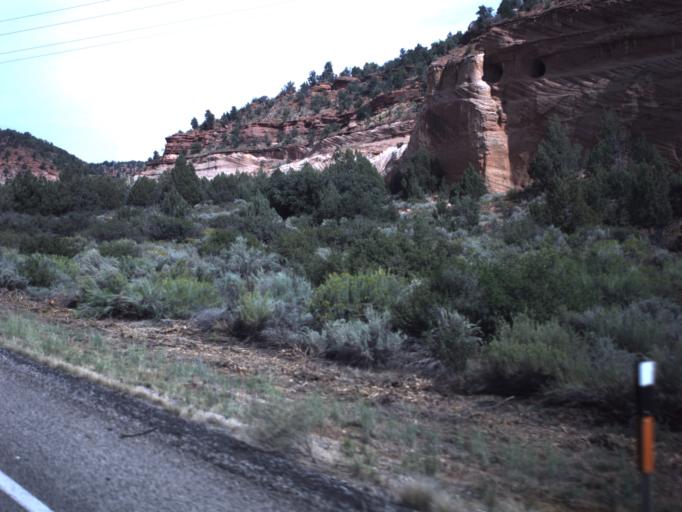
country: US
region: Utah
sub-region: Kane County
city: Kanab
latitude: 37.1149
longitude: -112.5601
